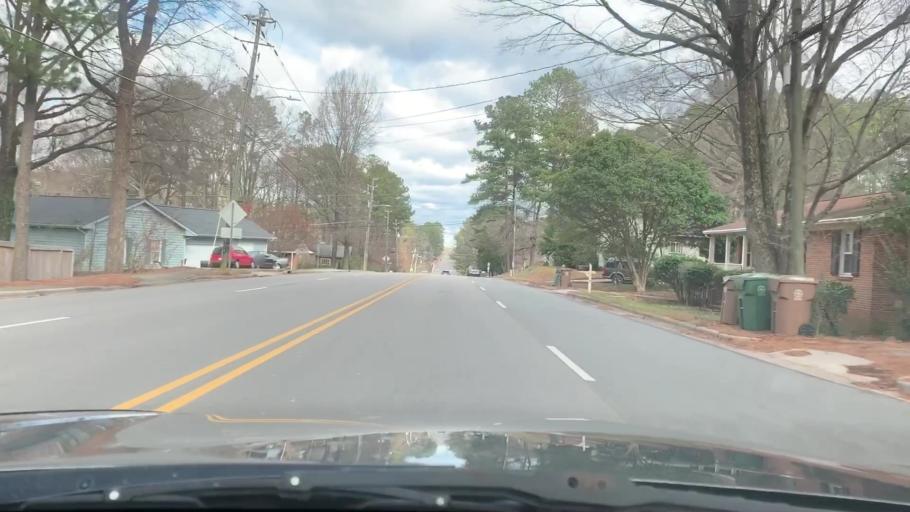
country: US
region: North Carolina
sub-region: Wake County
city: Cary
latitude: 35.7929
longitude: -78.7831
